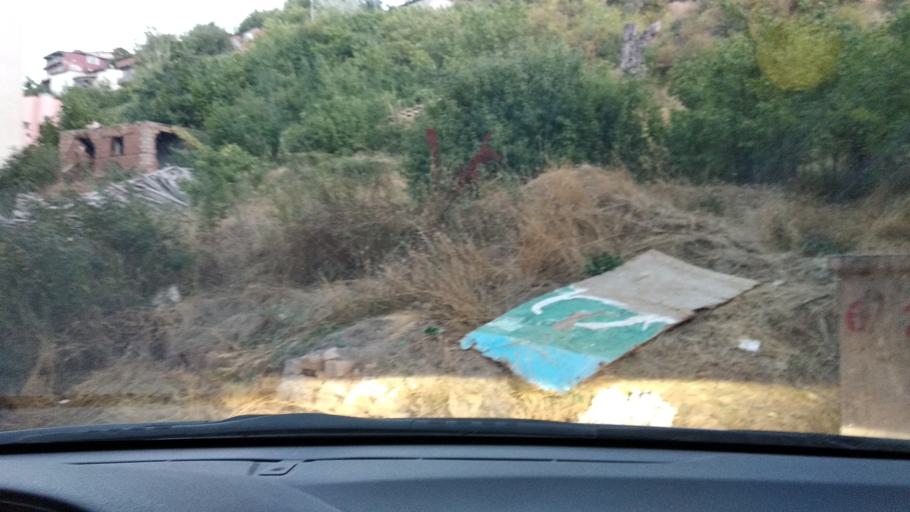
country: TR
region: Gumushane
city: Gumushkhane
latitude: 40.4567
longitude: 39.4838
